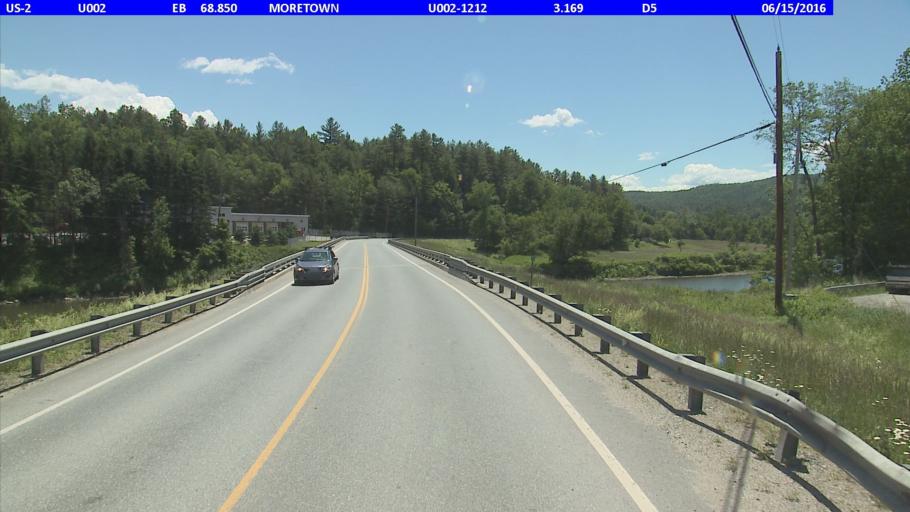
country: US
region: Vermont
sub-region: Washington County
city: Waterbury
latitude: 44.3070
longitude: -72.6967
